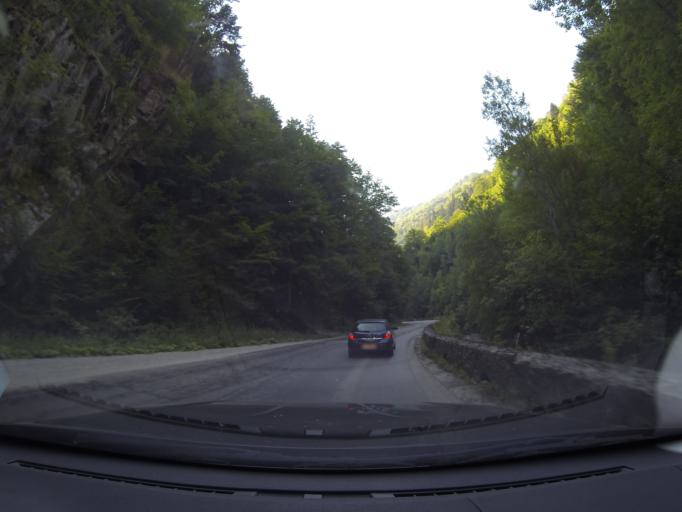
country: RO
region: Arges
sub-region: Comuna Arefu
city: Arefu
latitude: 45.3577
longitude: 24.6279
